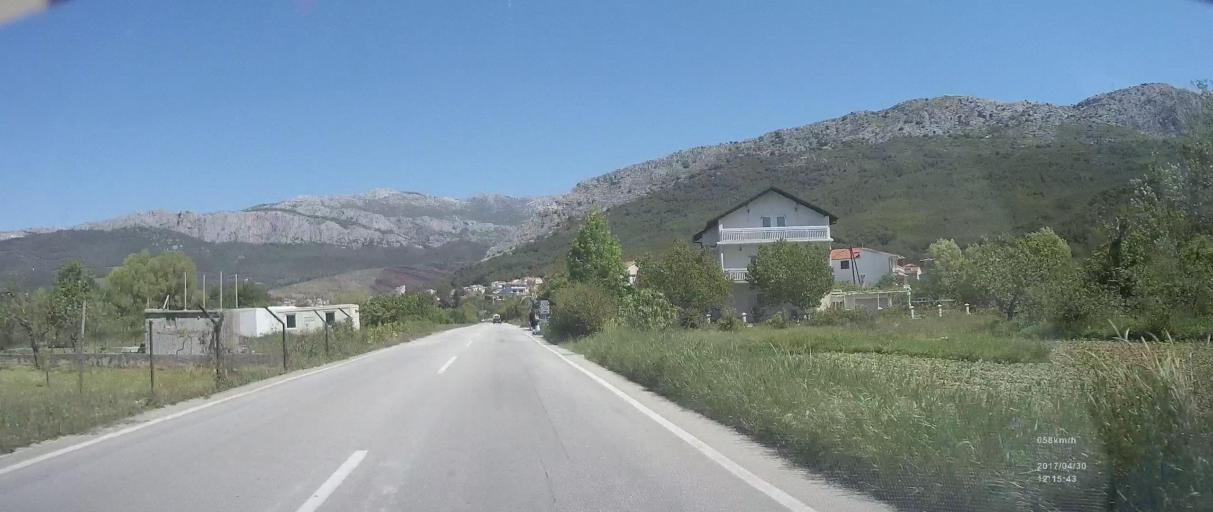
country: HR
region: Splitsko-Dalmatinska
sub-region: Grad Split
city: Stobrec
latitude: 43.5062
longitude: 16.5356
